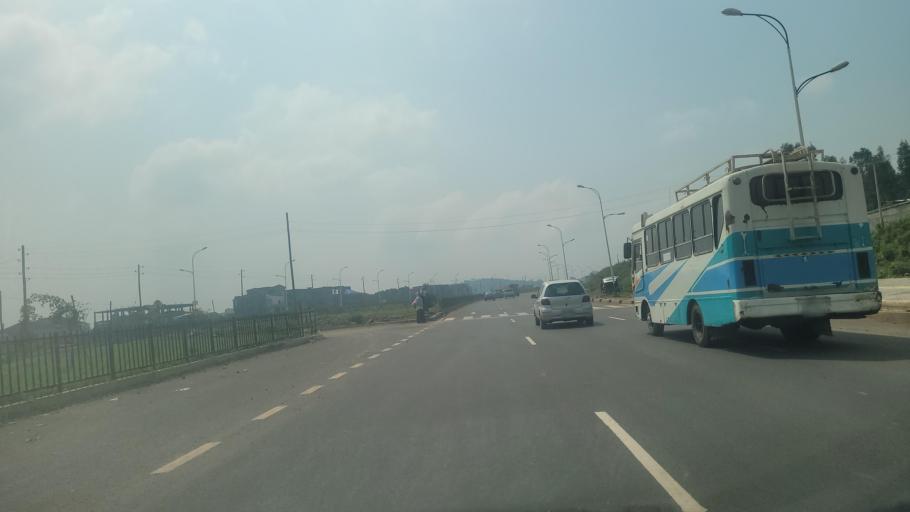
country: ET
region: Adis Abeba
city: Addis Ababa
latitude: 8.9485
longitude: 38.7107
